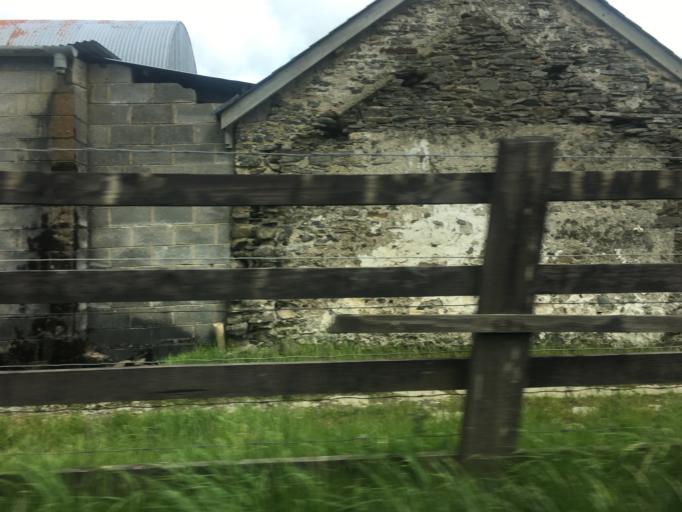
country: GB
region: Wales
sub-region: County of Ceredigion
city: Lampeter
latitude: 52.1265
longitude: -4.0760
